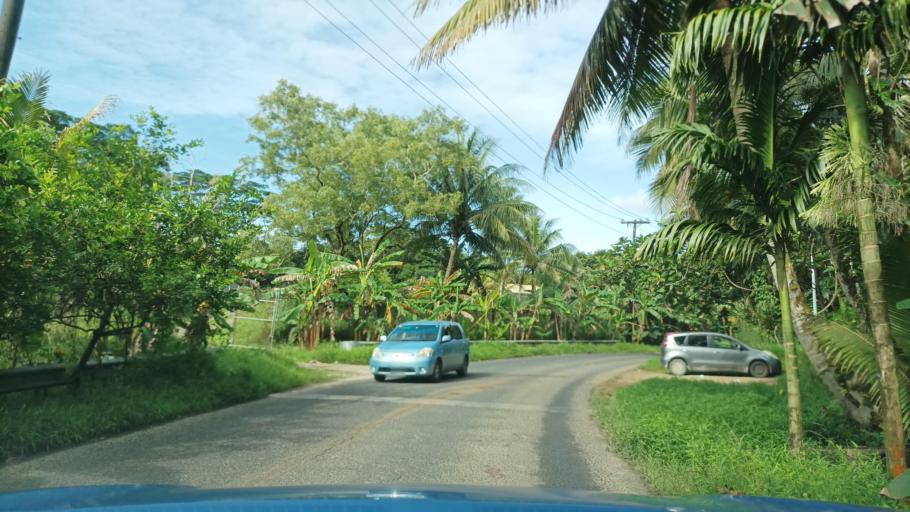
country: FM
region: Pohnpei
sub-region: Kolonia Municipality
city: Kolonia
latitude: 6.9518
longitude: 158.2335
